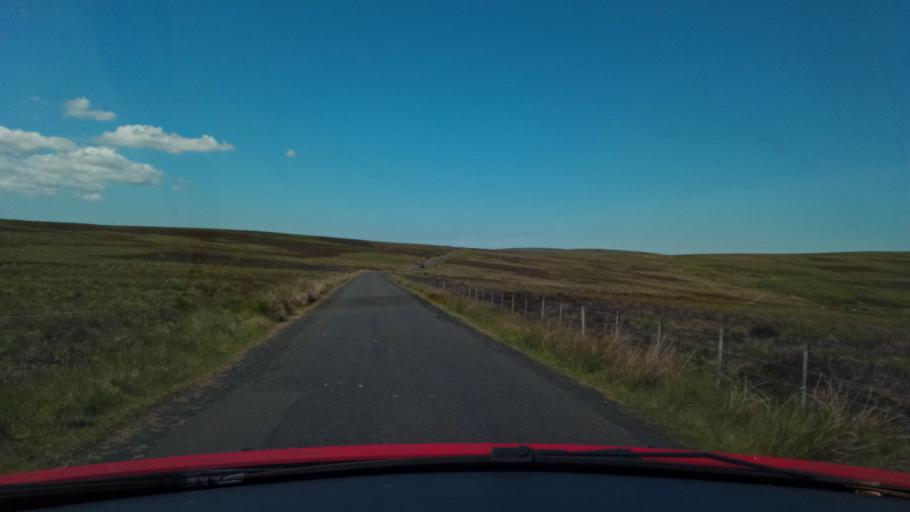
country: GB
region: Scotland
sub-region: East Lothian
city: Dunbar
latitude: 55.8376
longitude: -2.5501
